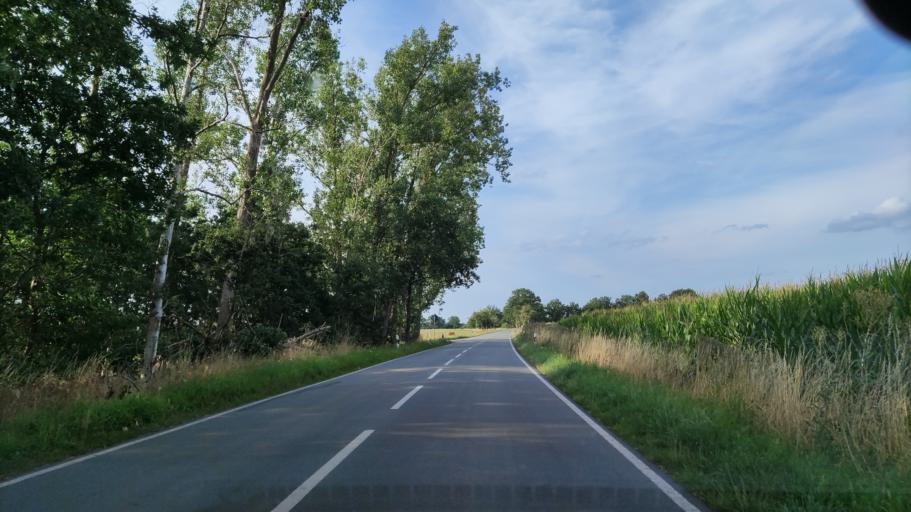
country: DE
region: Lower Saxony
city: Dannenberg
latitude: 53.1153
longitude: 11.1129
